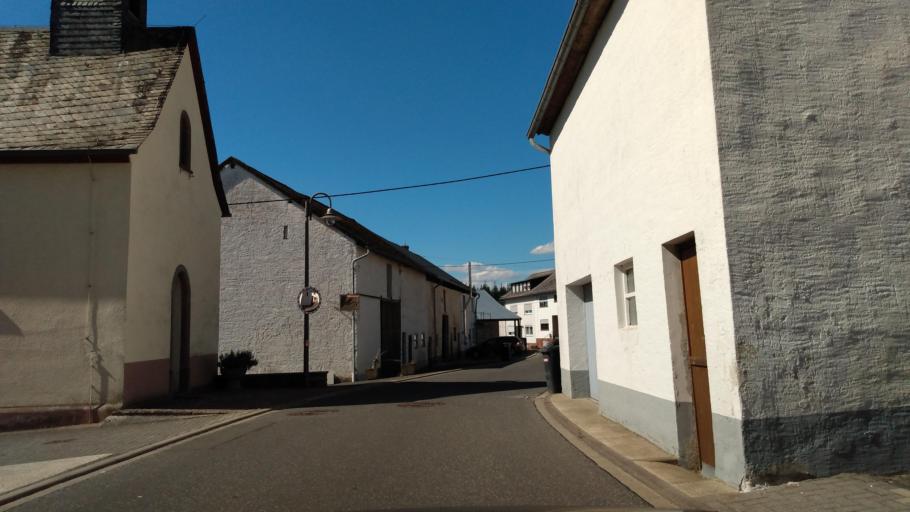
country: DE
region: Rheinland-Pfalz
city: Schwarzenborn
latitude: 50.0190
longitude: 6.7172
